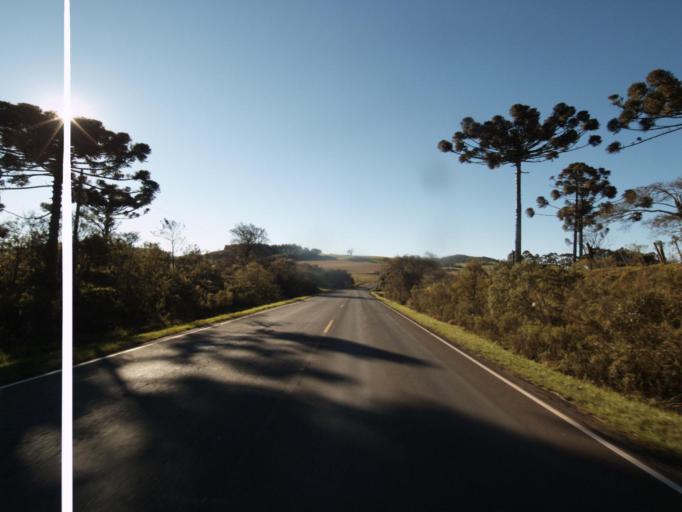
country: AR
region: Misiones
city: Bernardo de Irigoyen
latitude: -26.3454
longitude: -53.5465
